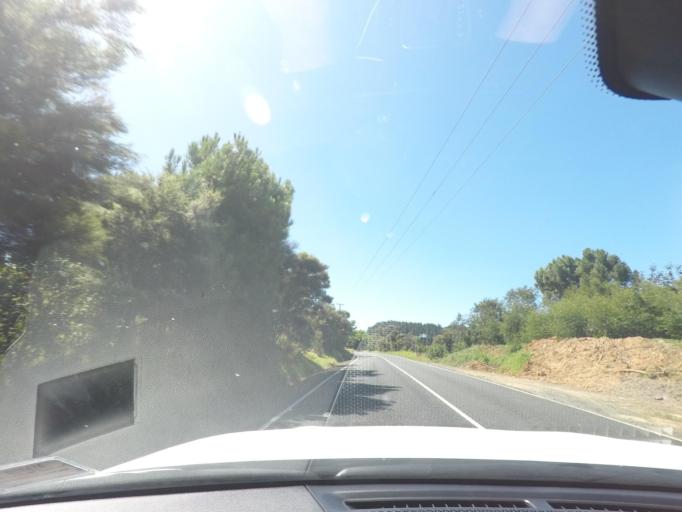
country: NZ
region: Auckland
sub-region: Auckland
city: Parakai
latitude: -36.5828
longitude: 174.3302
